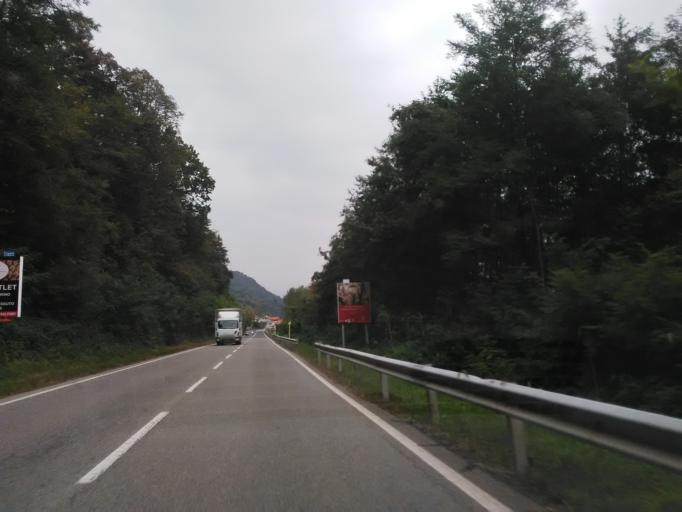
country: IT
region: Piedmont
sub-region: Provincia di Vercelli
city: Borgosesia
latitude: 45.7339
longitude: 8.2598
